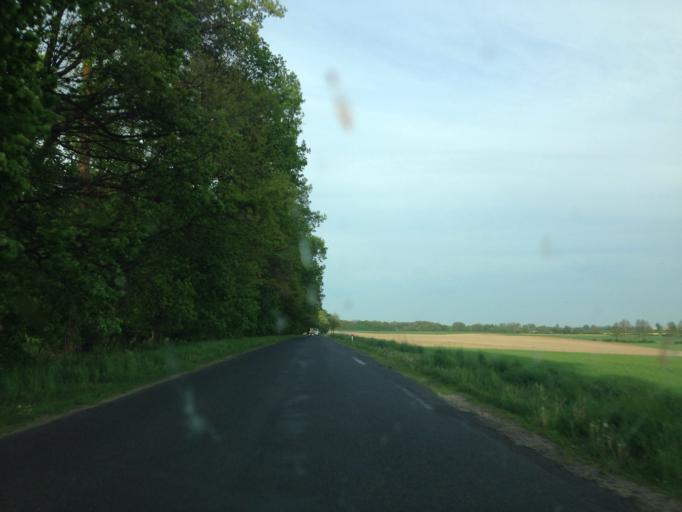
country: PL
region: Kujawsko-Pomorskie
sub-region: Powiat wabrzeski
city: Debowa Laka
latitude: 53.2586
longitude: 19.0633
